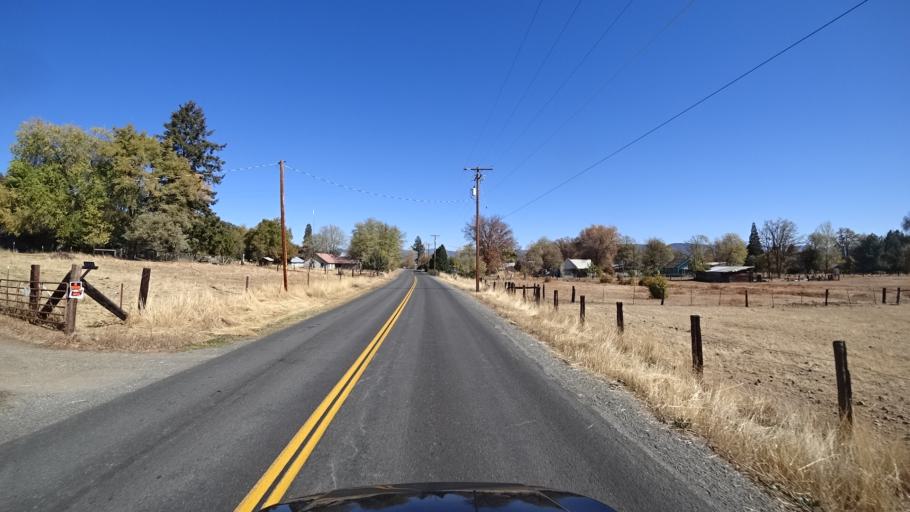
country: US
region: California
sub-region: Siskiyou County
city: Yreka
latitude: 41.5507
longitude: -122.9088
